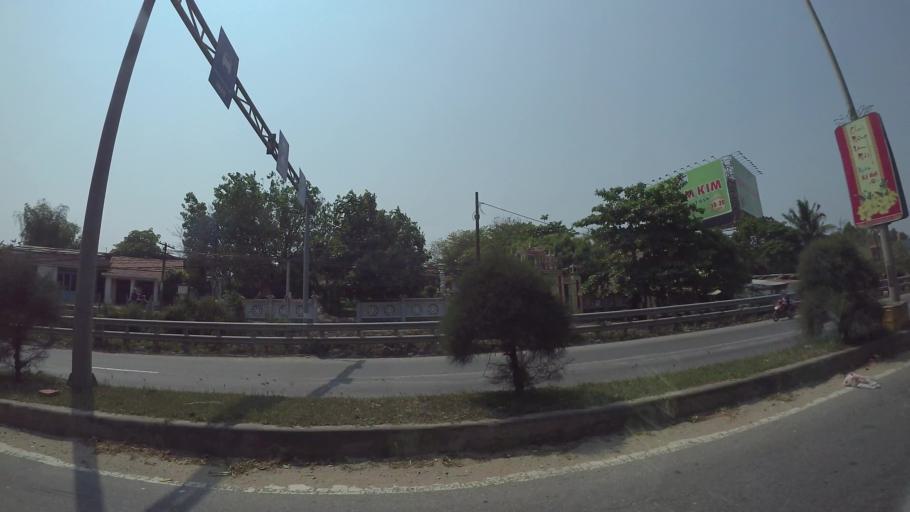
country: VN
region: Da Nang
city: Cam Le
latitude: 16.0127
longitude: 108.1929
